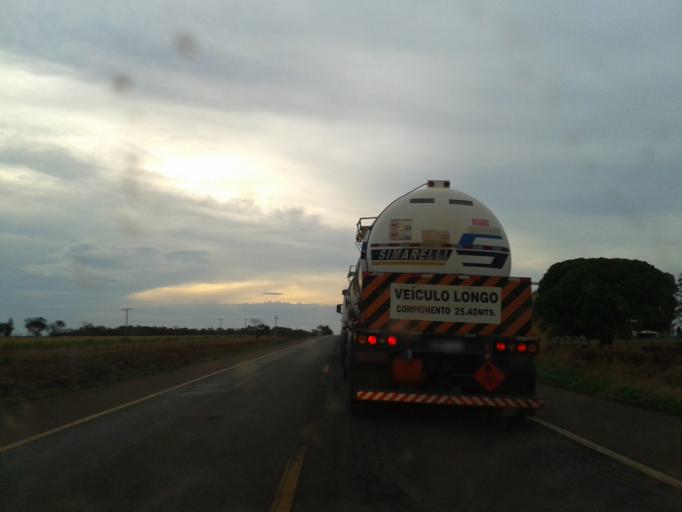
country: BR
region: Goias
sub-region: Santa Helena De Goias
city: Santa Helena de Goias
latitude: -17.9362
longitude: -50.5384
